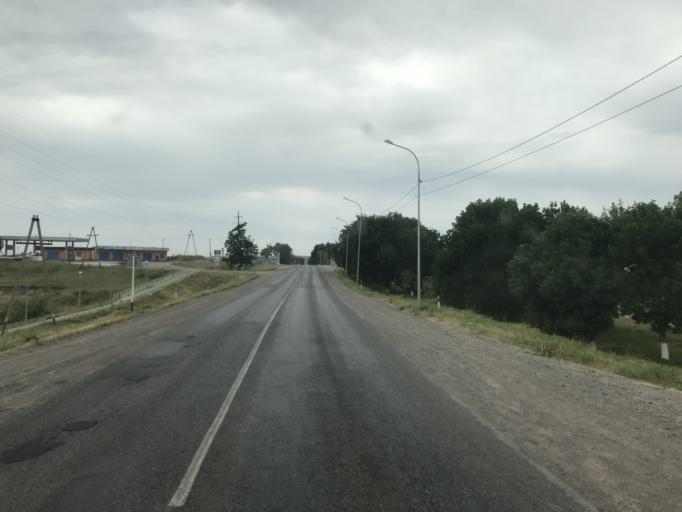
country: KZ
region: Ongtustik Qazaqstan
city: Saryaghash
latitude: 41.4914
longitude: 69.2886
